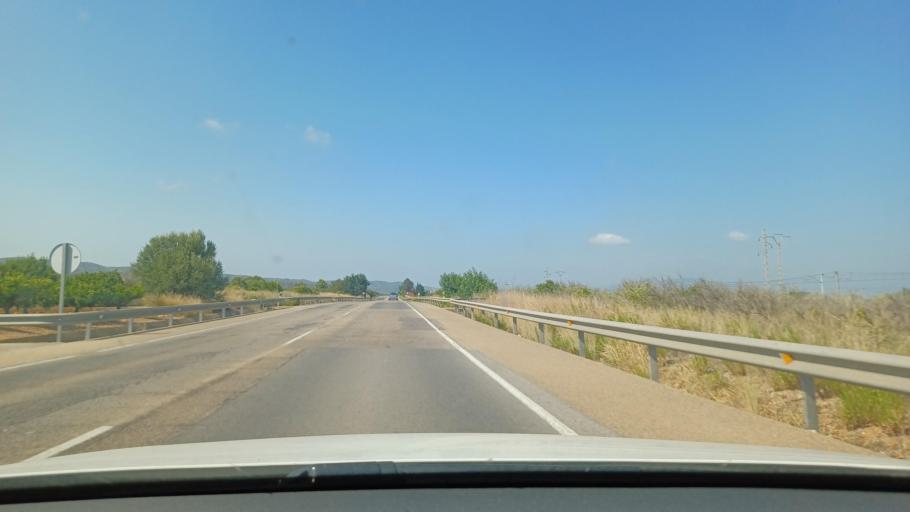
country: ES
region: Valencia
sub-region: Provincia de Castello
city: Torreblanca
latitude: 40.1697
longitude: 0.1663
